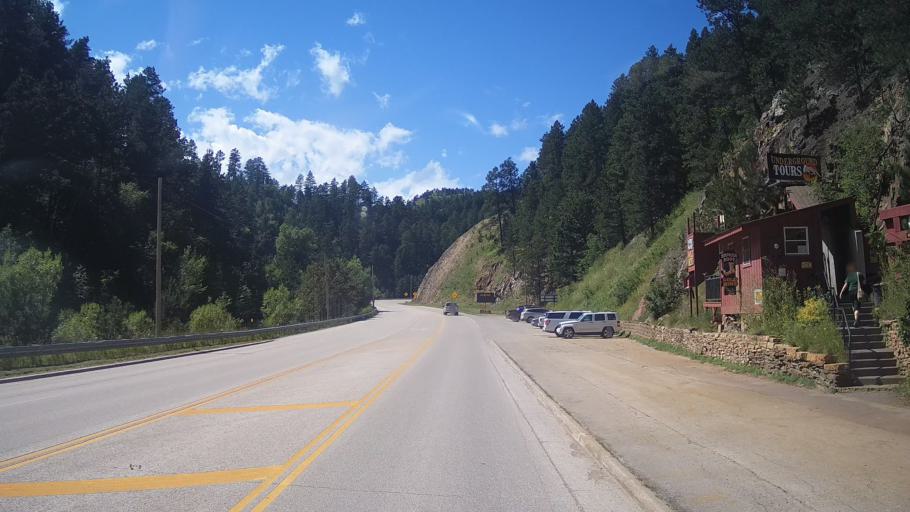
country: US
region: South Dakota
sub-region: Lawrence County
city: Deadwood
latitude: 44.3707
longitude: -103.7426
